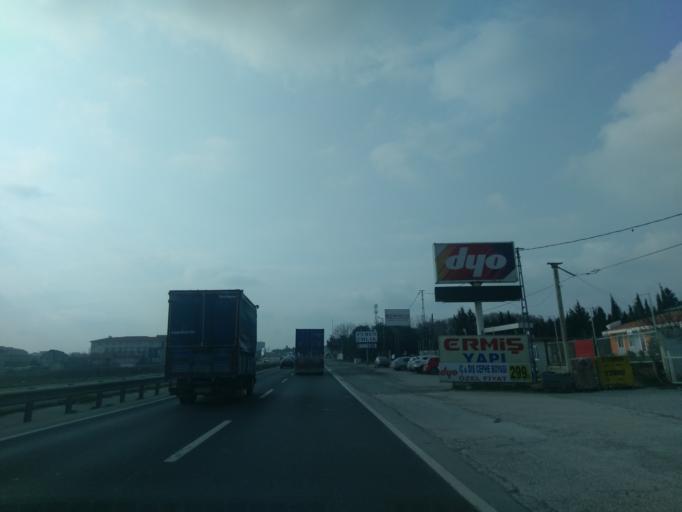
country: TR
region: Istanbul
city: Silivri
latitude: 41.0697
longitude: 28.2888
